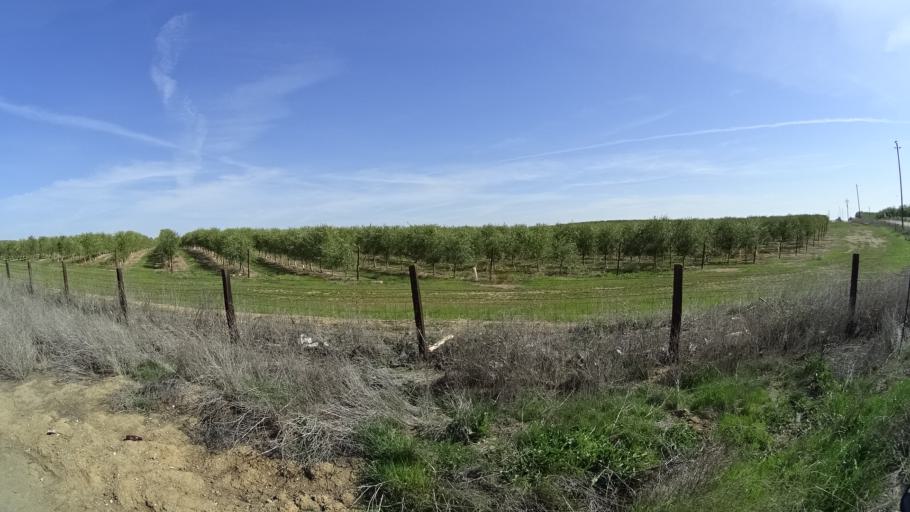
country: US
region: California
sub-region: Glenn County
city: Willows
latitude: 39.6116
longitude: -122.2869
